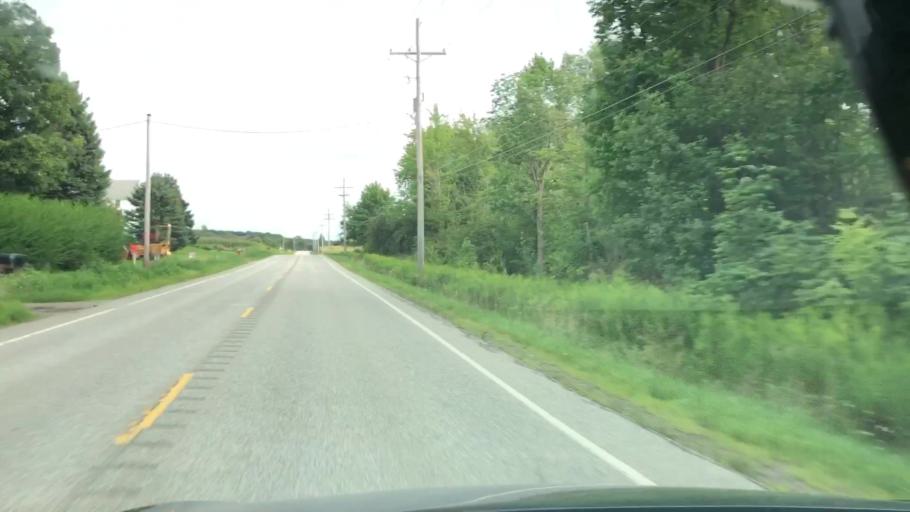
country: US
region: Pennsylvania
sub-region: Erie County
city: Union City
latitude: 41.9494
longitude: -79.8488
